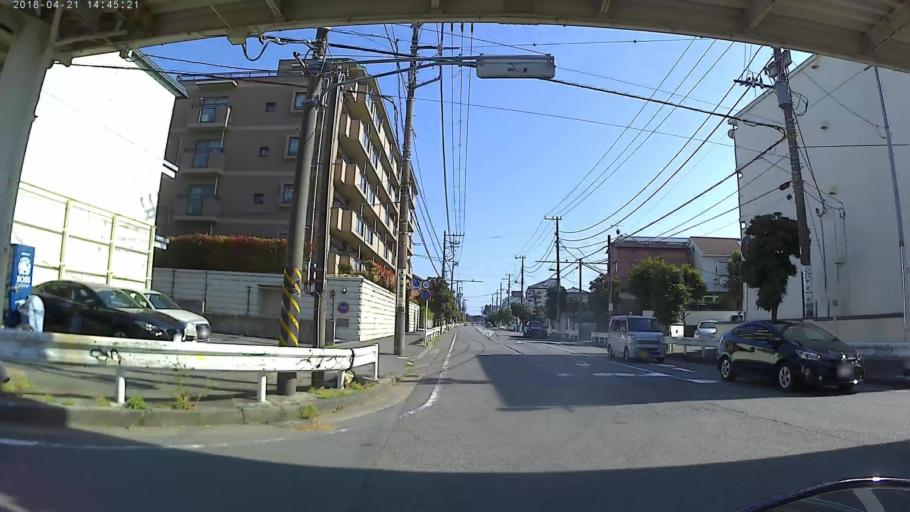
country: JP
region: Kanagawa
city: Hiratsuka
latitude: 35.3199
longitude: 139.3473
